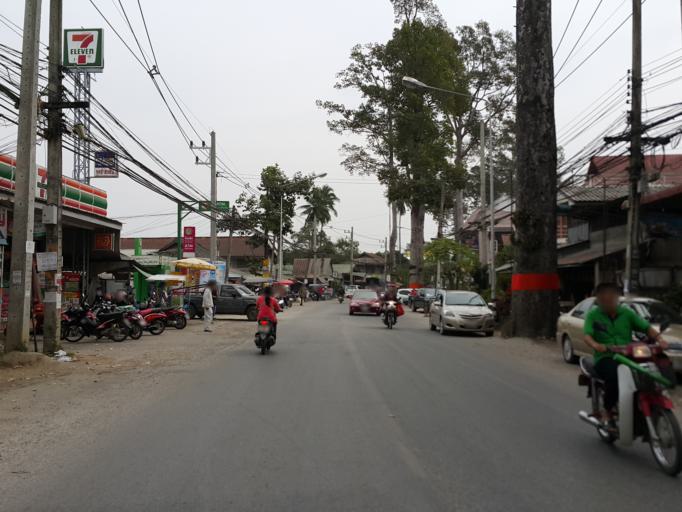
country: TH
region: Chiang Mai
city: Saraphi
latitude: 18.7151
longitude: 99.0339
